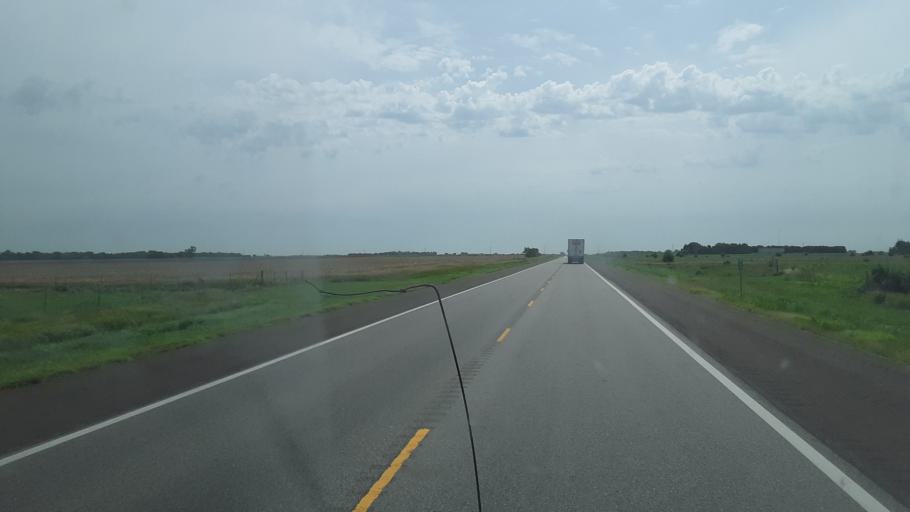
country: US
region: Kansas
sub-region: Reno County
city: Nickerson
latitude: 37.9850
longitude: -98.1156
